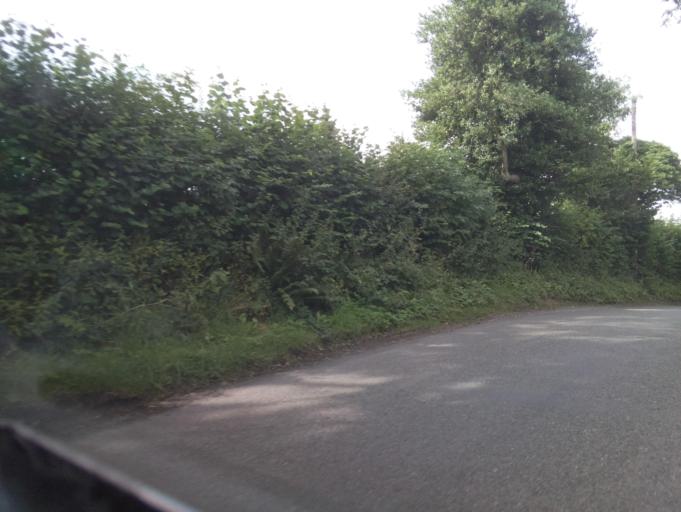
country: GB
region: England
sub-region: Somerset
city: Chilcompton
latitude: 51.2212
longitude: -2.5110
